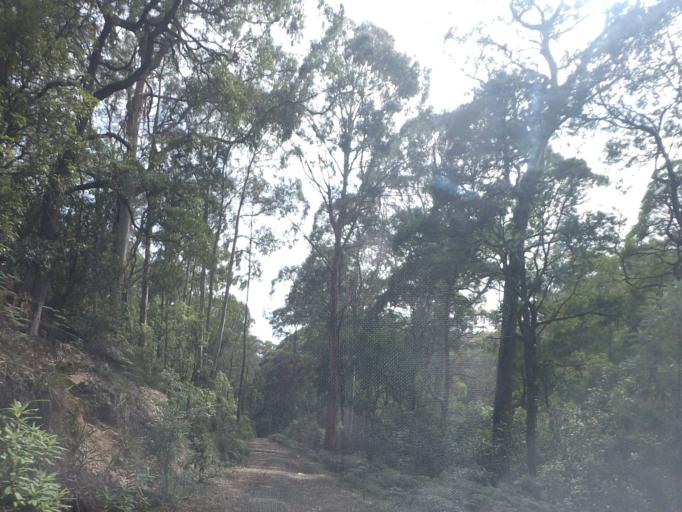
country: AU
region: Victoria
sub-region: Moorabool
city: Bacchus Marsh
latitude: -37.4361
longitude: 144.2613
